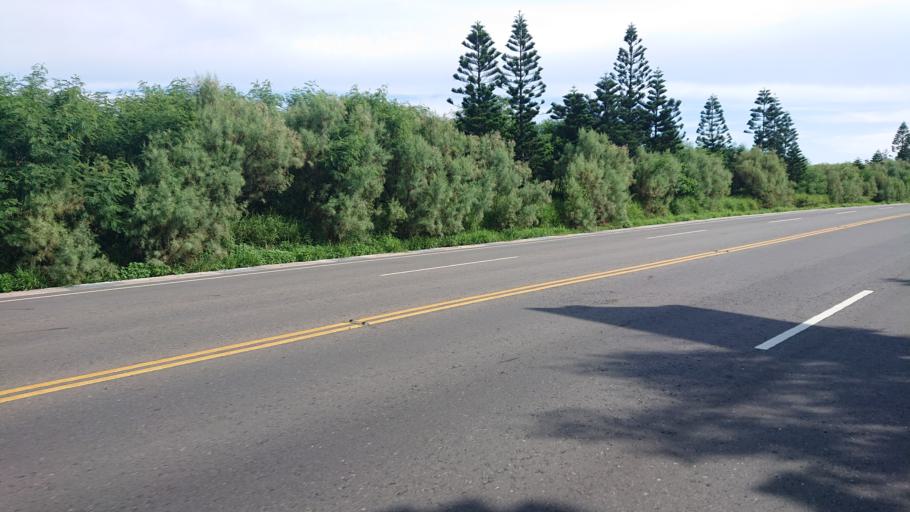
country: TW
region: Taiwan
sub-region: Penghu
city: Ma-kung
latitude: 23.5247
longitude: 119.5855
